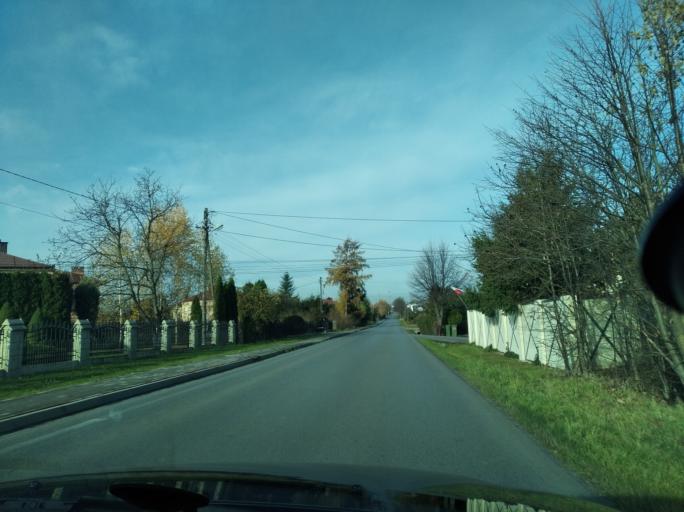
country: PL
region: Subcarpathian Voivodeship
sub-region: Powiat rzeszowski
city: Krasne
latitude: 50.0343
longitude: 22.0875
